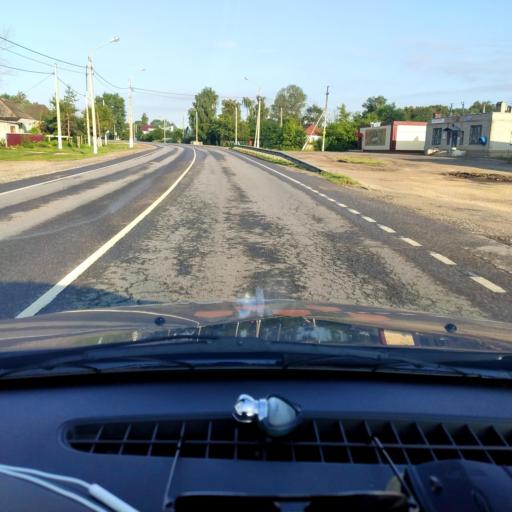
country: RU
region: Lipetsk
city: Kazaki
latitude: 52.5687
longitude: 38.1848
